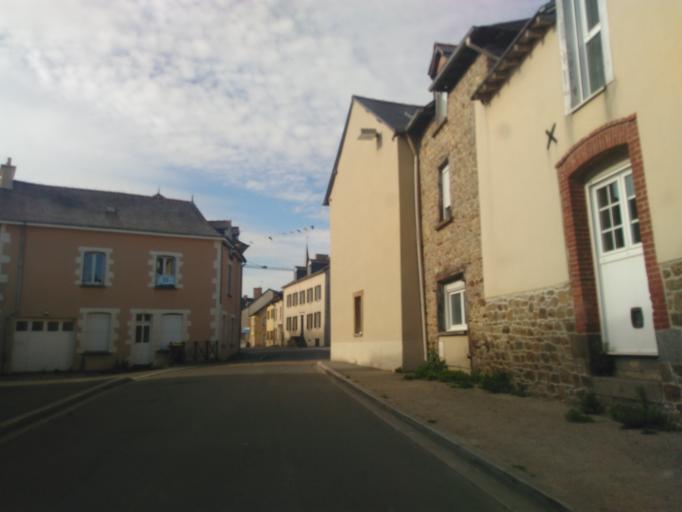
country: FR
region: Brittany
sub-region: Departement d'Ille-et-Vilaine
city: Romille
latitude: 48.2142
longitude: -1.8926
